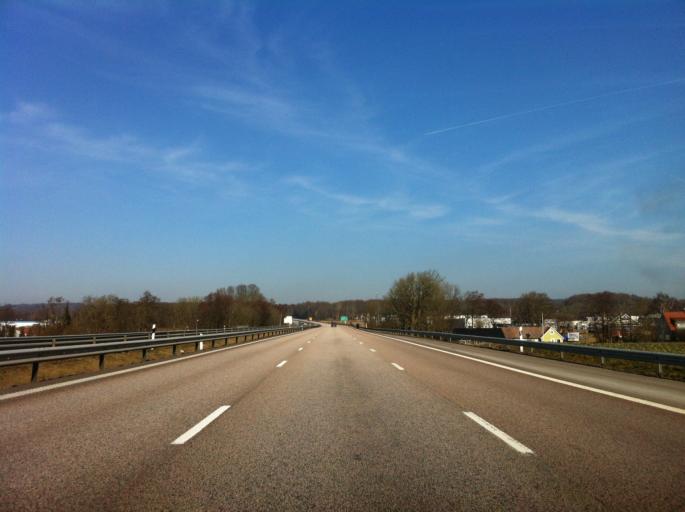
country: SE
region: Skane
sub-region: Angelholms Kommun
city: Munka-Ljungby
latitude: 56.3161
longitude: 12.9125
